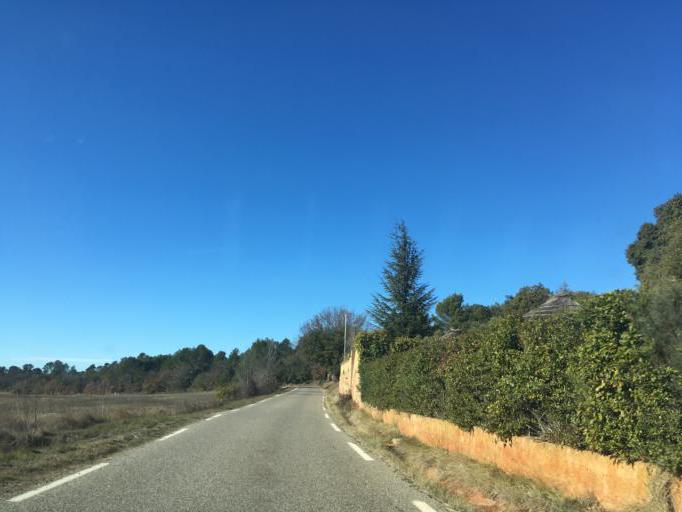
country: FR
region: Provence-Alpes-Cote d'Azur
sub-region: Departement du Var
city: Barjols
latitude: 43.5936
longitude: 6.0627
